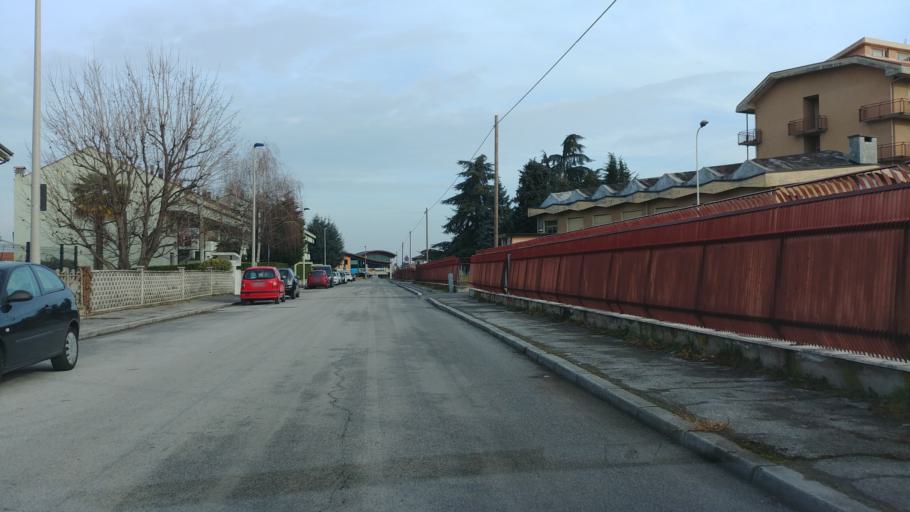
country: IT
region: Piedmont
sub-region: Provincia di Cuneo
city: Cuneo
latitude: 44.3897
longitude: 7.5664
